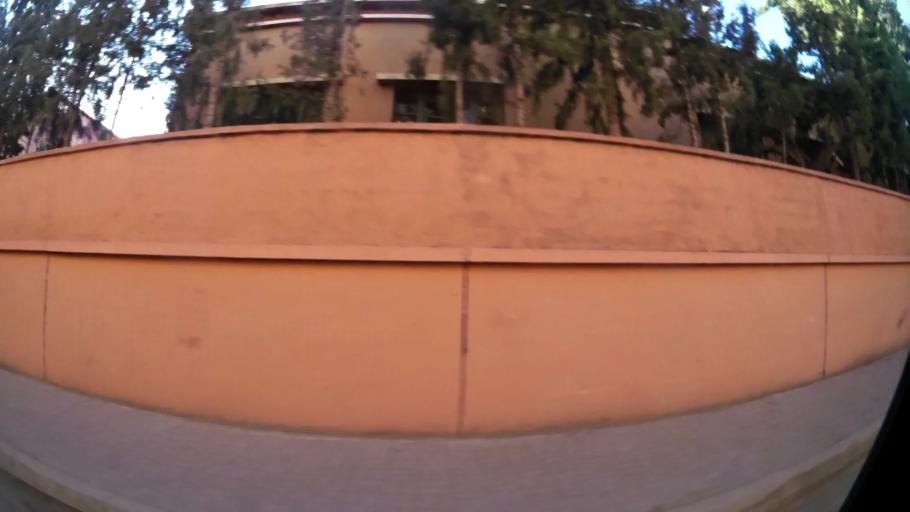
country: MA
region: Marrakech-Tensift-Al Haouz
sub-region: Marrakech
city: Marrakesh
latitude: 31.6192
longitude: -8.0643
